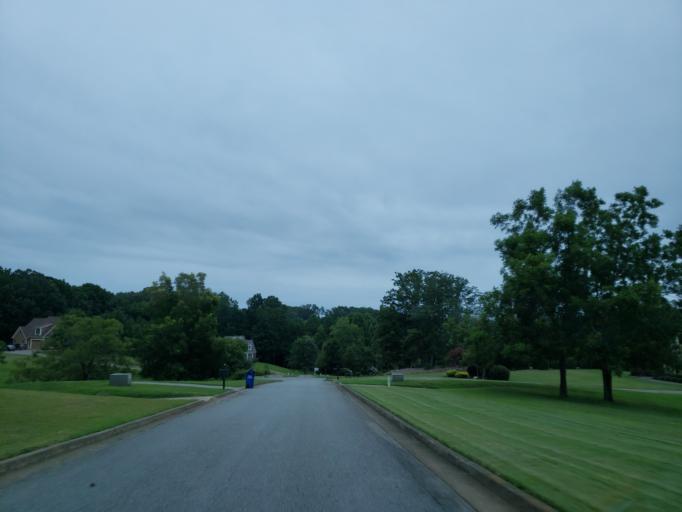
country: US
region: Georgia
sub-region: Cherokee County
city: Canton
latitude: 34.3281
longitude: -84.4725
